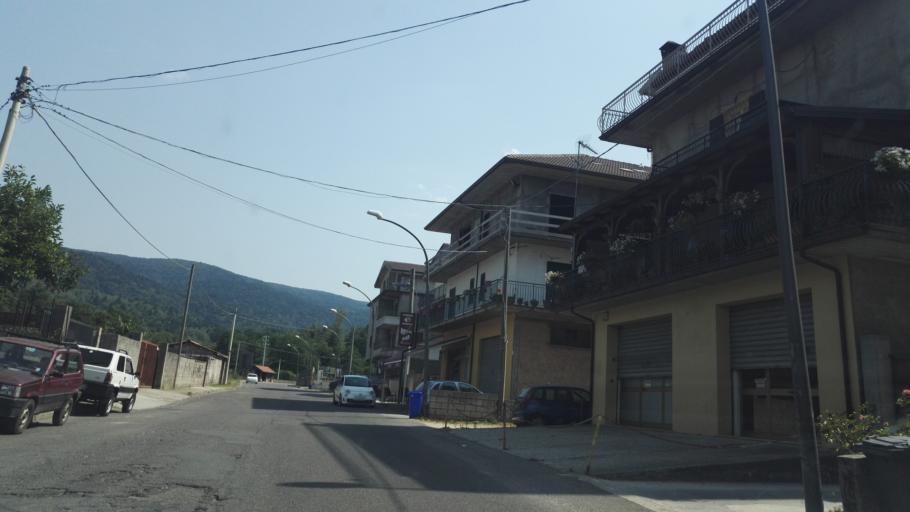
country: IT
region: Calabria
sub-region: Provincia di Vibo-Valentia
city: Serra San Bruno
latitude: 38.5668
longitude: 16.3282
